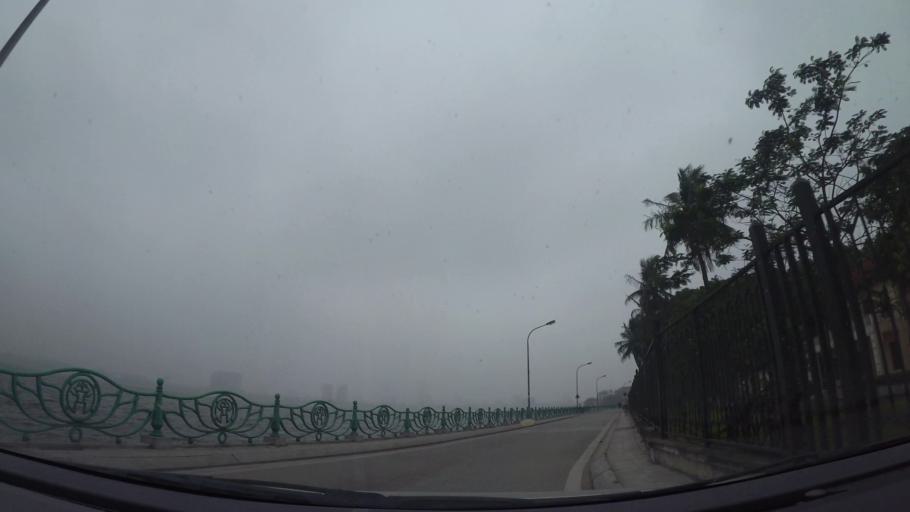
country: VN
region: Ha Noi
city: Tay Ho
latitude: 21.0583
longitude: 105.8252
